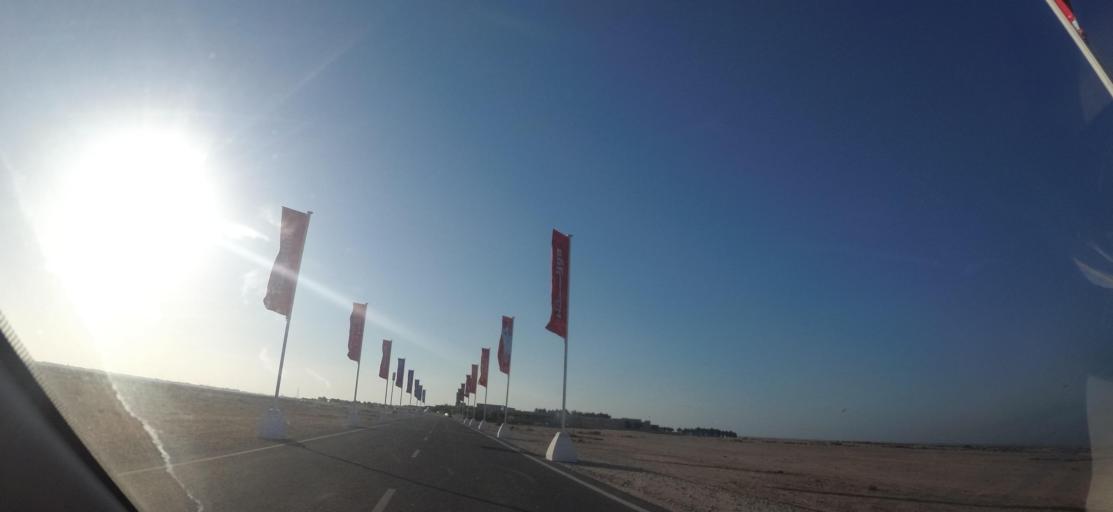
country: QA
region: Madinat ash Shamal
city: Ar Ru'ays
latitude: 26.1549
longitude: 51.2476
